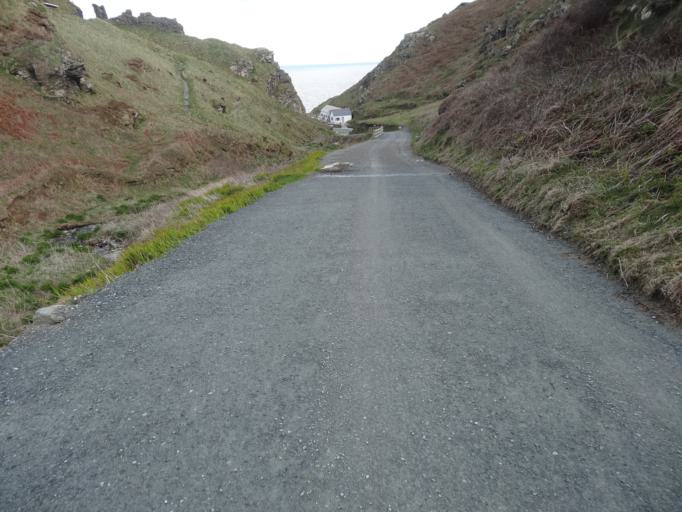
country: GB
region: England
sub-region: Cornwall
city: Tintagel
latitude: 50.6661
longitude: -4.7570
